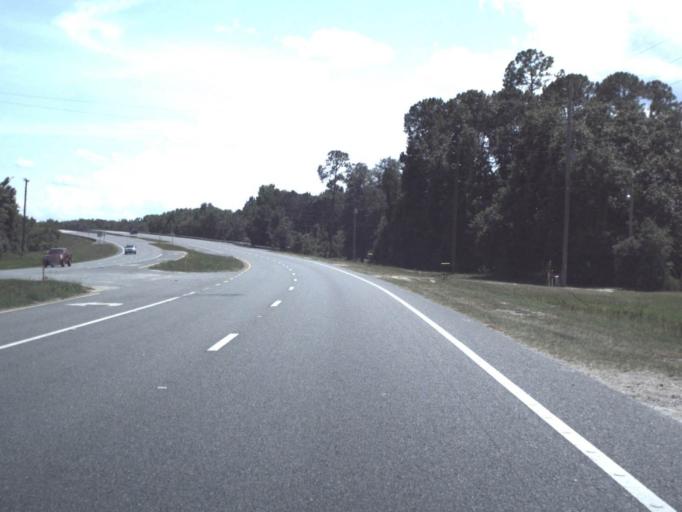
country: US
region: Florida
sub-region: Putnam County
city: Palatka
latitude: 29.7054
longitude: -81.6636
